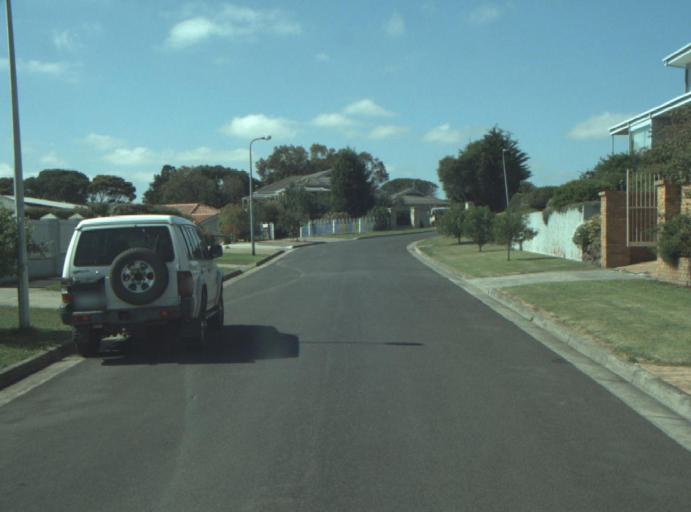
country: AU
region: Victoria
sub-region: Greater Geelong
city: Wandana Heights
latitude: -38.1608
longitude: 144.3144
